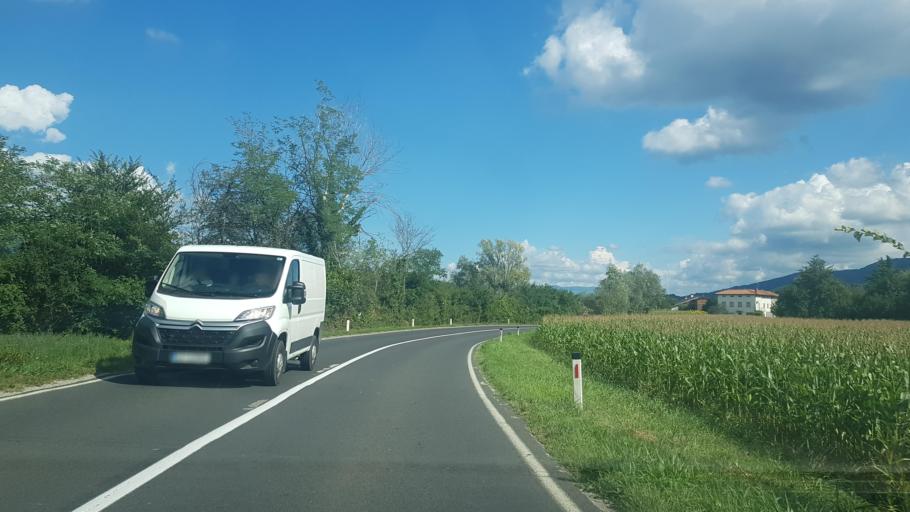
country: SI
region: Rence-Vogrsko
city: Volcja Draga
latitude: 45.8996
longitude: 13.6834
